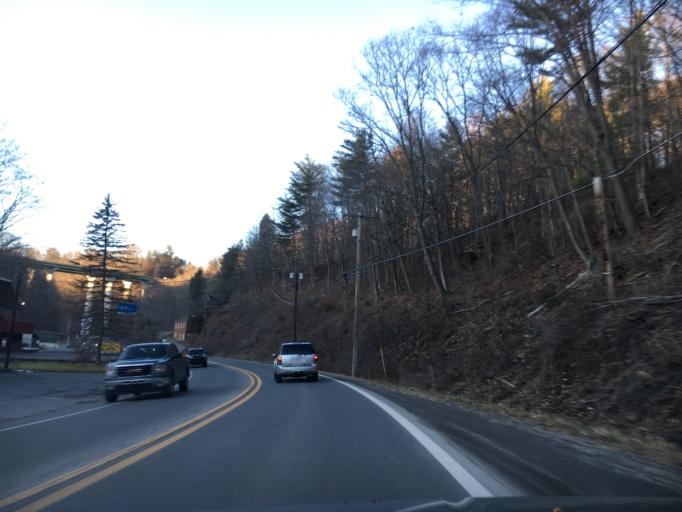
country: US
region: West Virginia
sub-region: Raleigh County
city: Beaver
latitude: 37.7522
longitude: -81.1478
